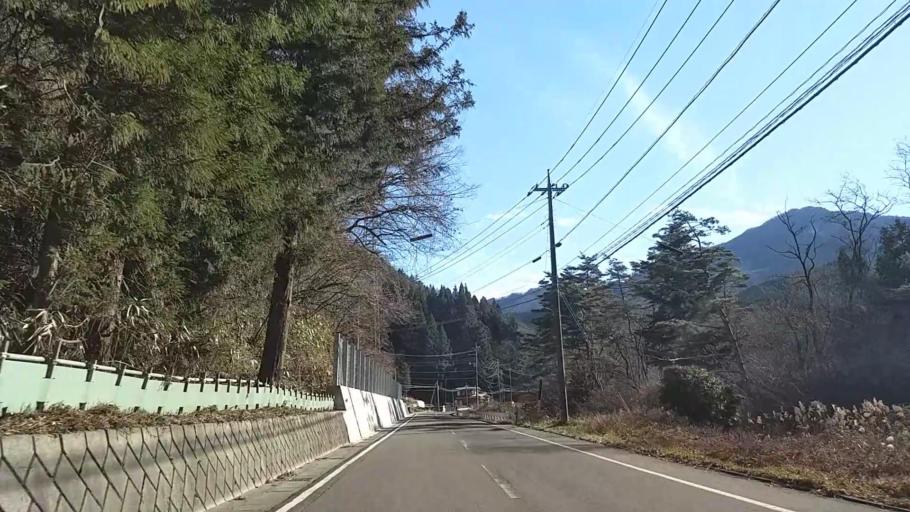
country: JP
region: Yamanashi
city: Otsuki
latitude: 35.5242
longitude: 138.9250
